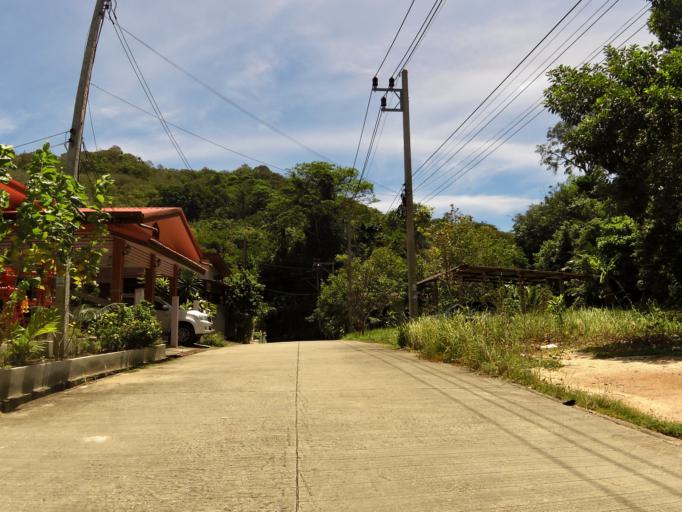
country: TH
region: Phuket
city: Ban Karon
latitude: 7.8489
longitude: 98.3071
